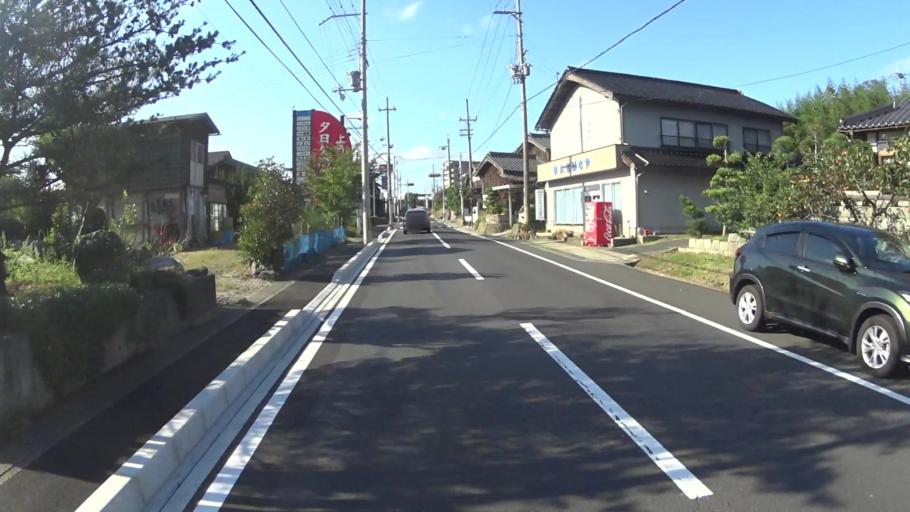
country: JP
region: Hyogo
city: Toyooka
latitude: 35.6560
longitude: 134.9685
